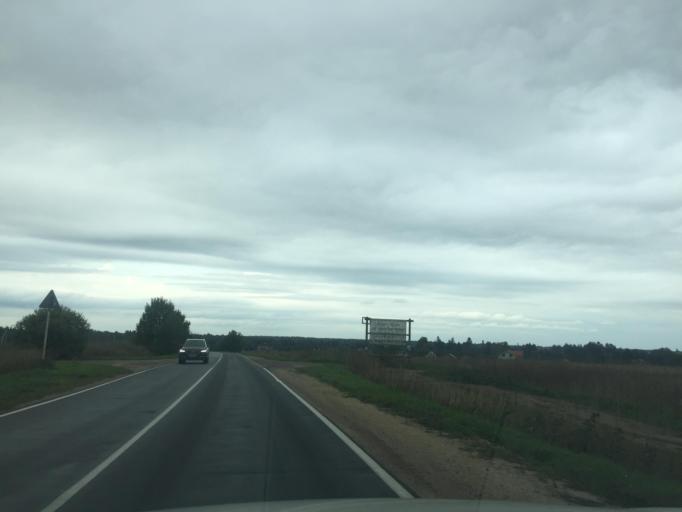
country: RU
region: Leningrad
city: Siverskiy
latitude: 59.3343
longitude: 30.0312
